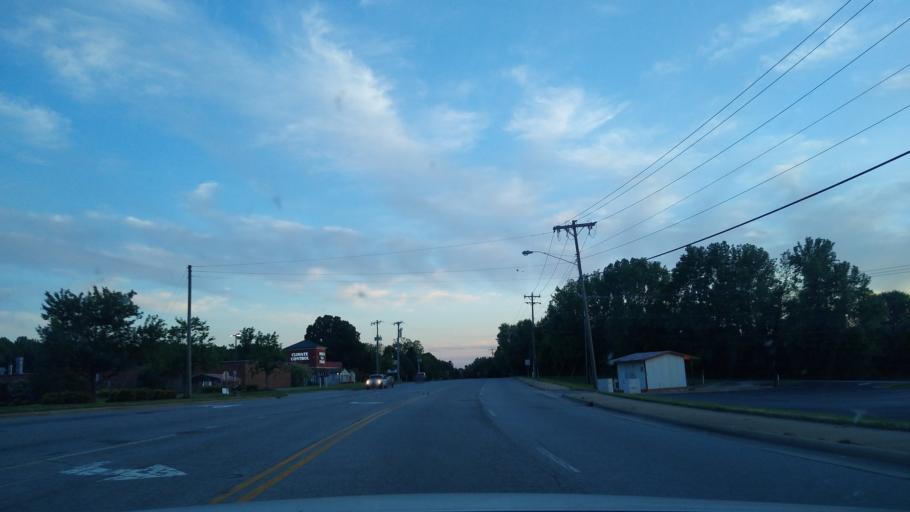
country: US
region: North Carolina
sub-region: Guilford County
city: Jamestown
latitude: 36.0598
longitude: -79.9092
